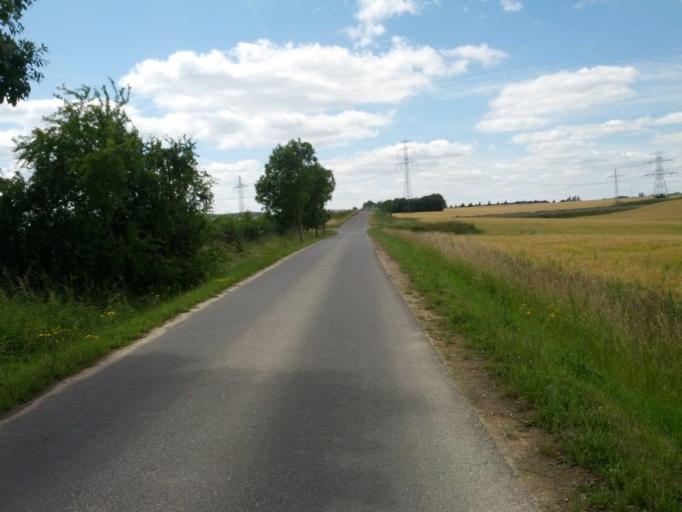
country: DE
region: Thuringia
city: Bischofroda
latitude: 51.0156
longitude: 10.3825
